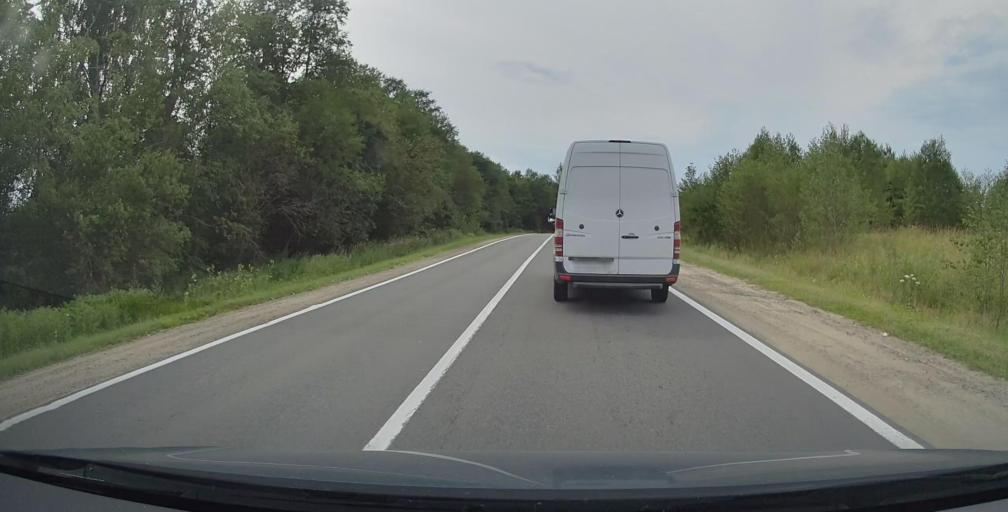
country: RU
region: Jaroslavl
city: Rybinsk
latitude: 57.9774
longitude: 38.7471
